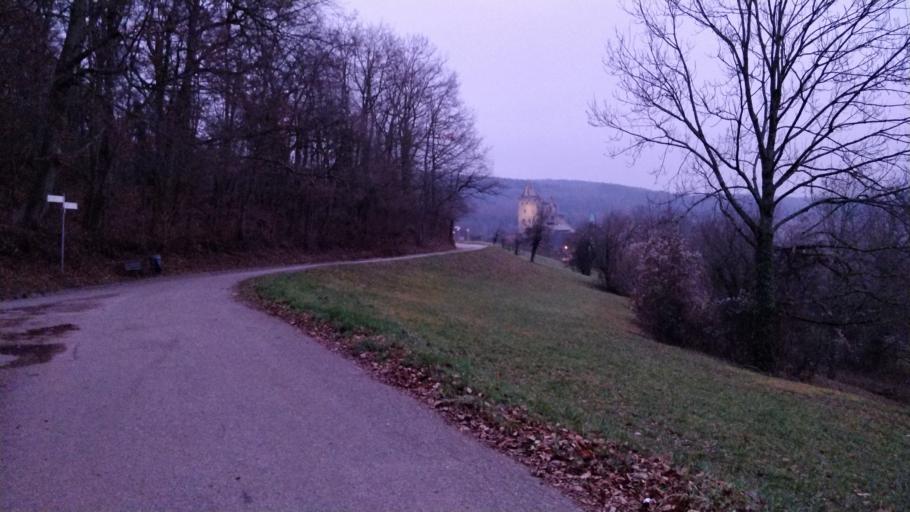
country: DE
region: Baden-Wuerttemberg
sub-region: Freiburg Region
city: Teningen
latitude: 48.1523
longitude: 7.8375
